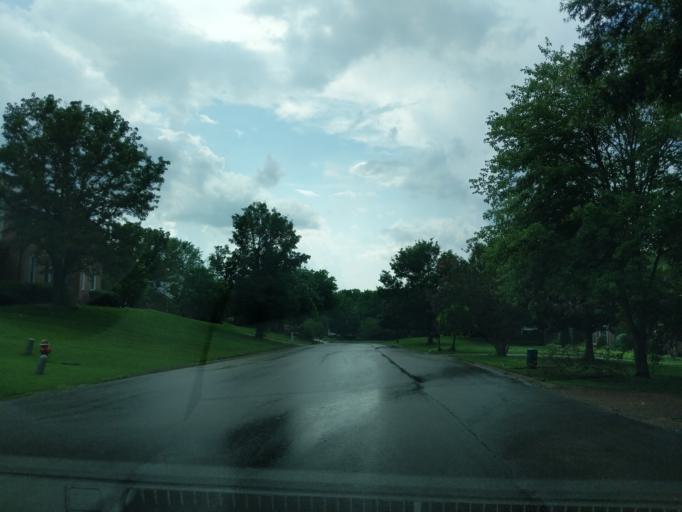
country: US
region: Tennessee
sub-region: Davidson County
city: Belle Meade
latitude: 36.0446
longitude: -86.9453
